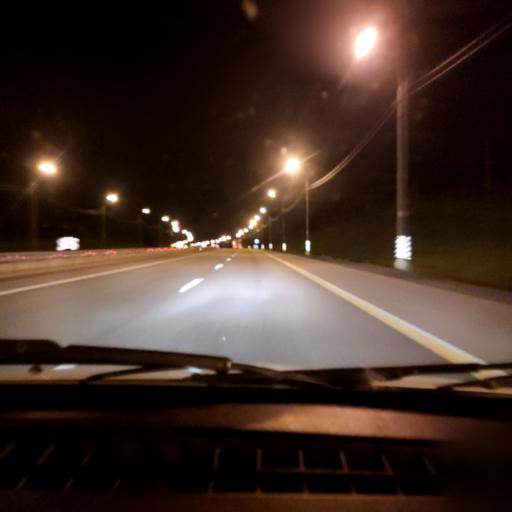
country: RU
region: Lipetsk
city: Khlevnoye
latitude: 52.2970
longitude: 39.0518
